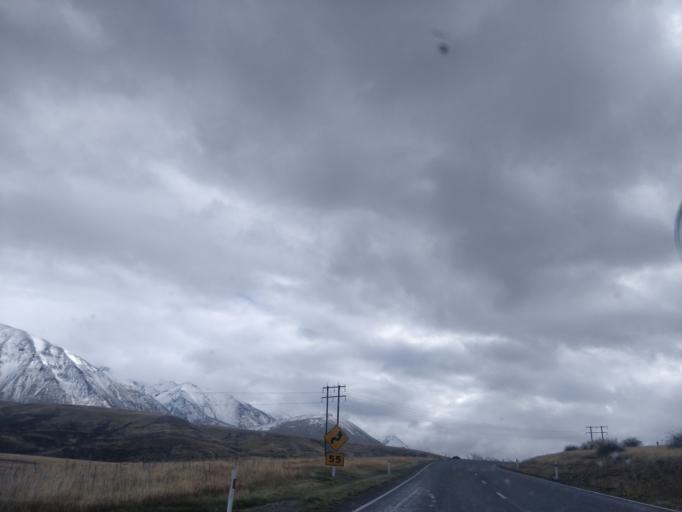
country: NZ
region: Canterbury
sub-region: Ashburton District
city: Methven
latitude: -43.2607
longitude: 171.7118
